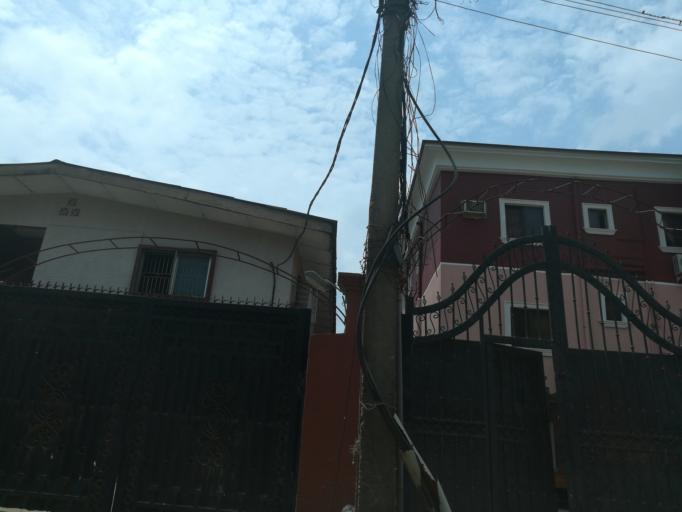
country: NG
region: Lagos
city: Oshodi
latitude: 6.5515
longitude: 3.3262
